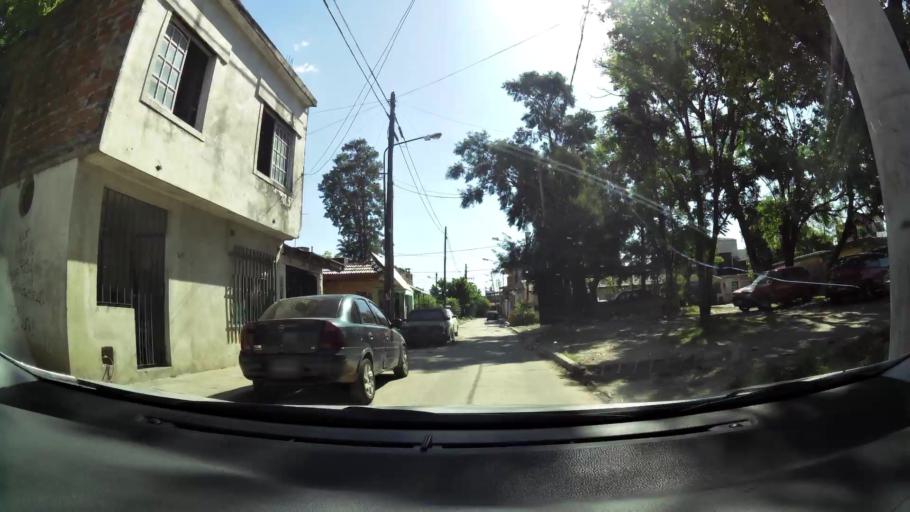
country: AR
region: Buenos Aires F.D.
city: Villa Lugano
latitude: -34.7080
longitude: -58.4771
